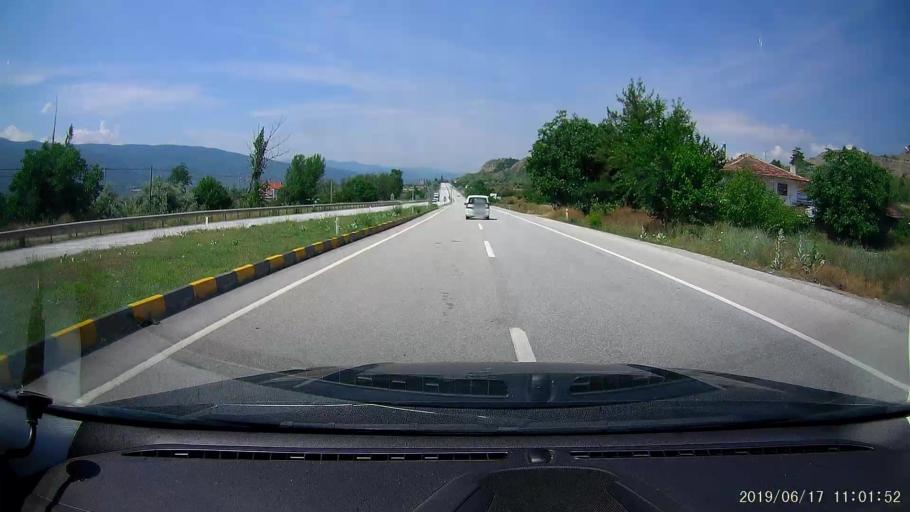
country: TR
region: Kastamonu
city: Tosya
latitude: 41.0235
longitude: 34.1467
